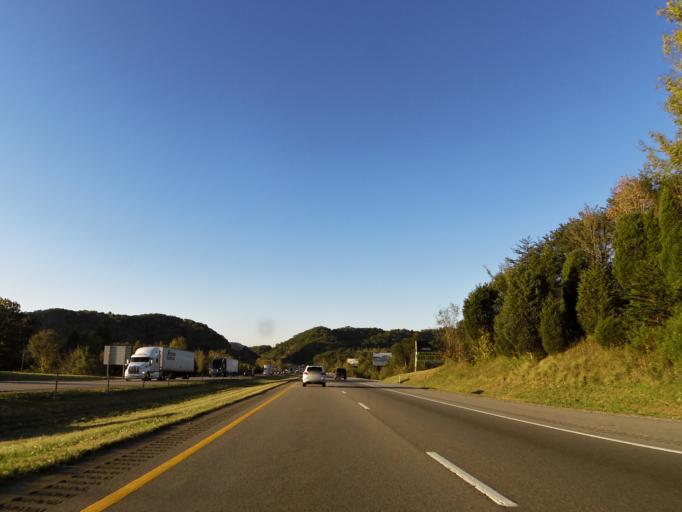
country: US
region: Tennessee
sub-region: Anderson County
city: Norris
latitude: 36.1226
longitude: -84.0349
